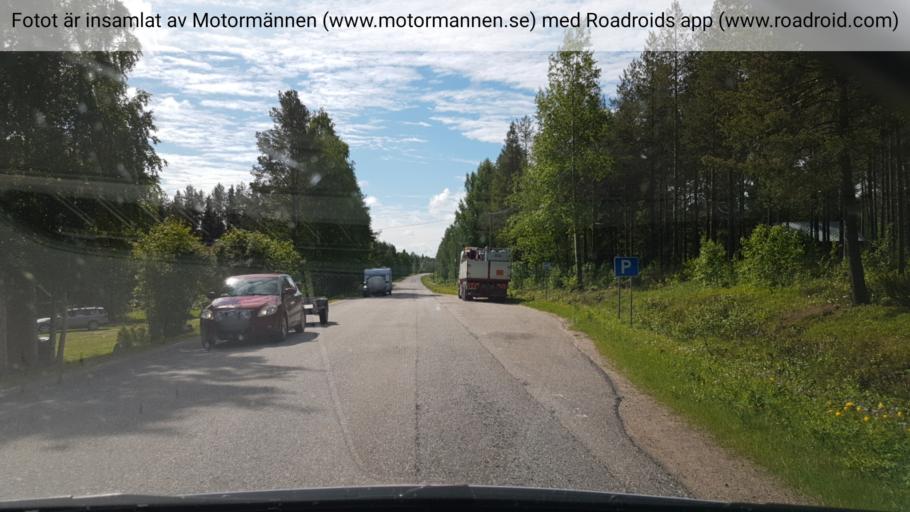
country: FI
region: Lapland
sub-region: Torniolaakso
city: Pello
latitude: 66.5961
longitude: 23.8570
